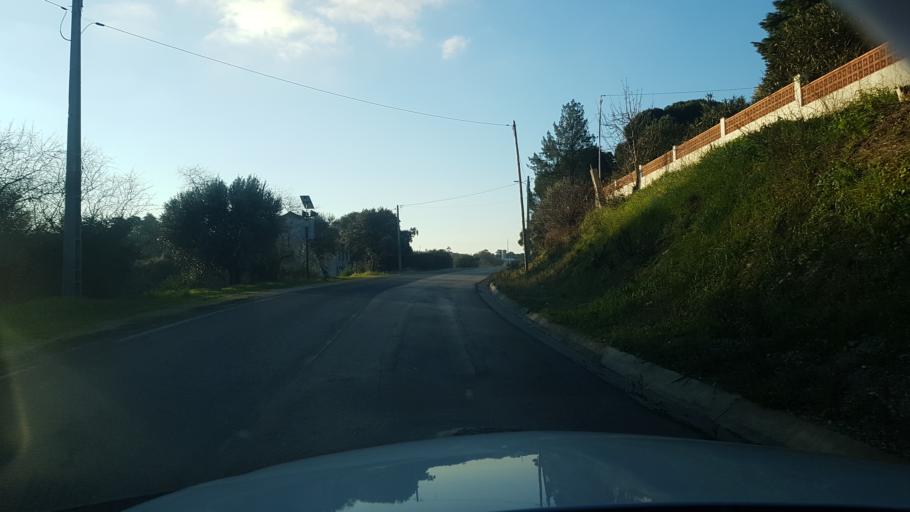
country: PT
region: Santarem
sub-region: Torres Novas
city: Torres Novas
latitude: 39.5512
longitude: -8.5521
